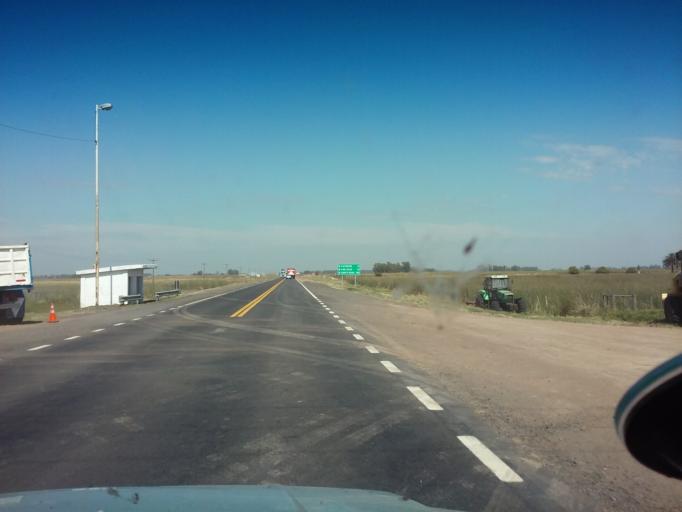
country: AR
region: Buenos Aires
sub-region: Partido de Nueve de Julio
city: Nueve de Julio
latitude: -35.3698
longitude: -60.7138
